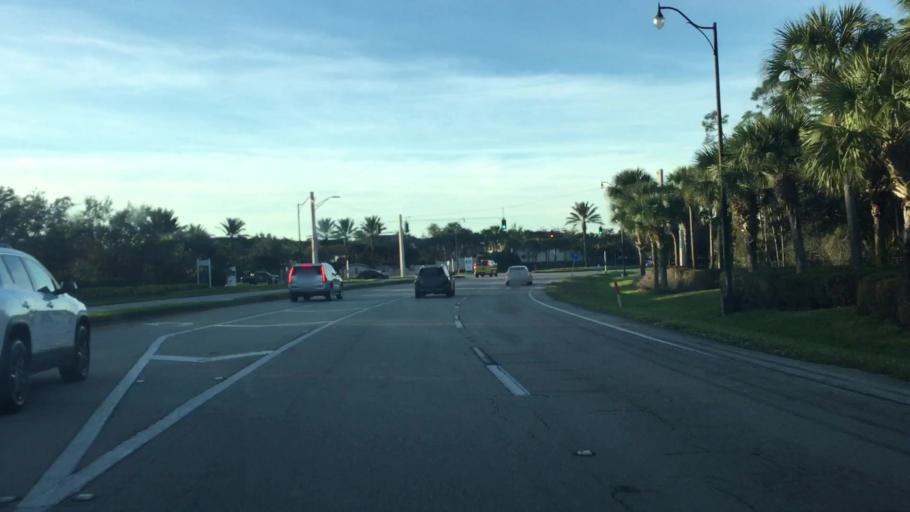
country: US
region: Florida
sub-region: Lee County
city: Gateway
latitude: 26.6052
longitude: -81.7842
